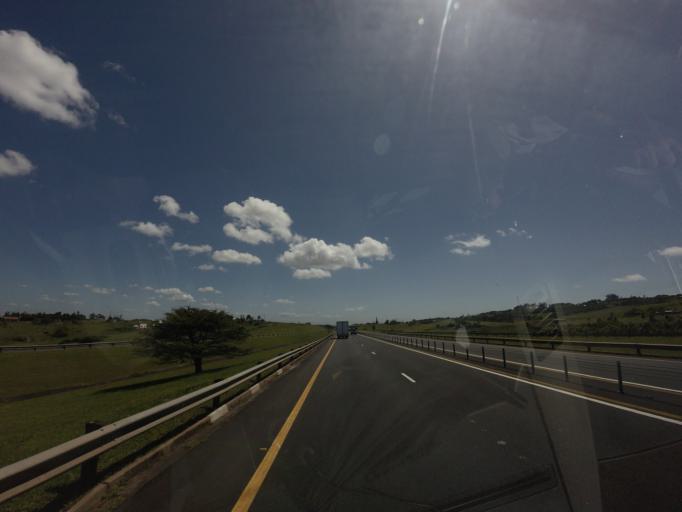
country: ZA
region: KwaZulu-Natal
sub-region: iLembe District Municipality
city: Mandeni
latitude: -29.0756
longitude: 31.6161
